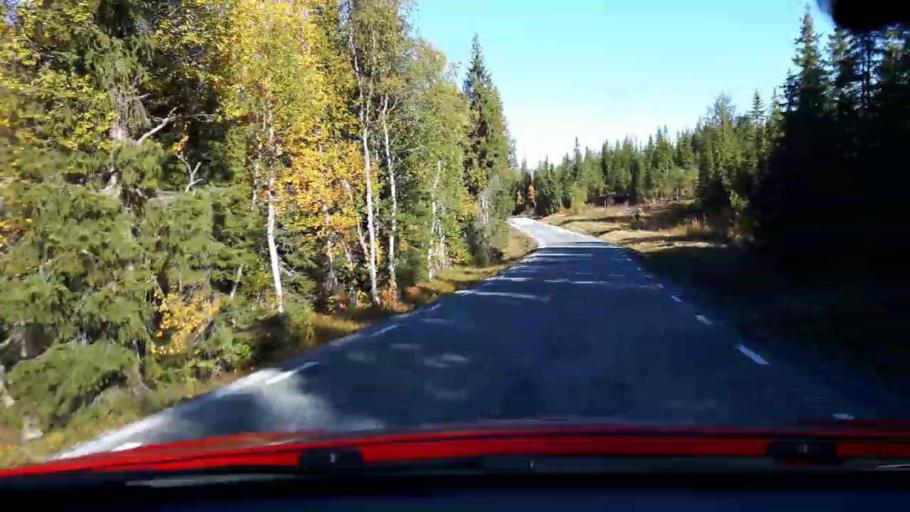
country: NO
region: Nord-Trondelag
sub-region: Lierne
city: Sandvika
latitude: 64.6195
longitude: 13.6974
